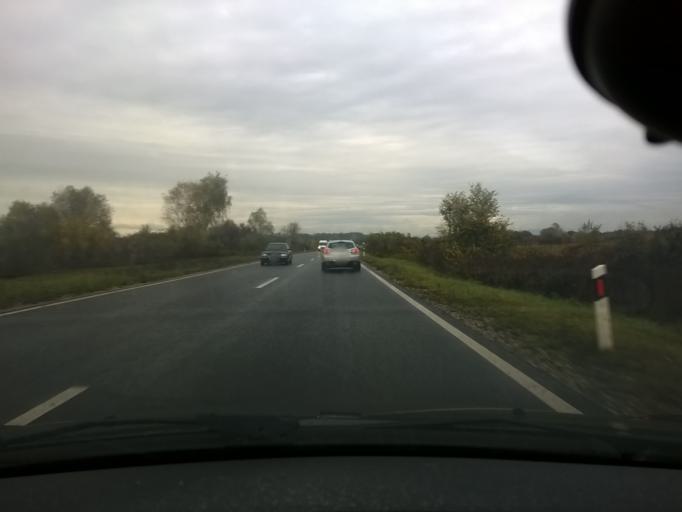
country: HR
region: Zagrebacka
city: Jakovlje
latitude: 45.9388
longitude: 15.8214
